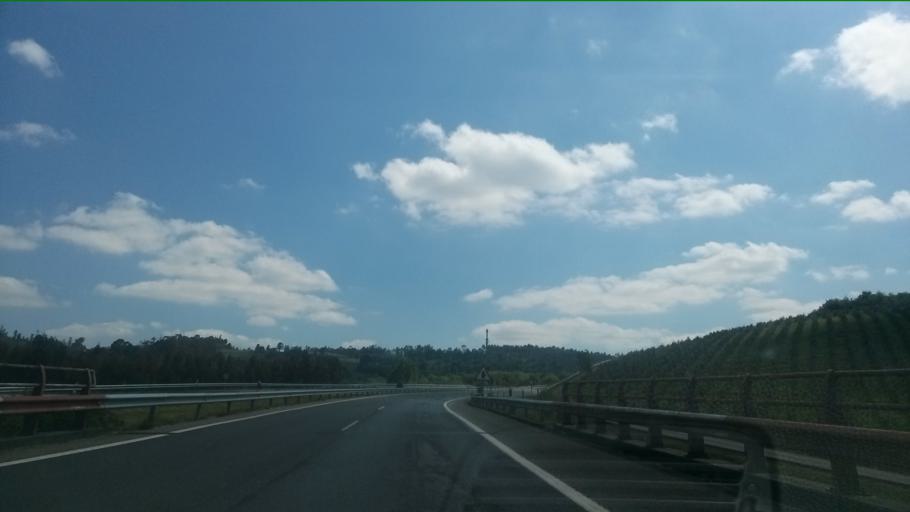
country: ES
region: Galicia
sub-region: Provincia da Coruna
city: Oroso
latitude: 42.9067
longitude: -8.4629
